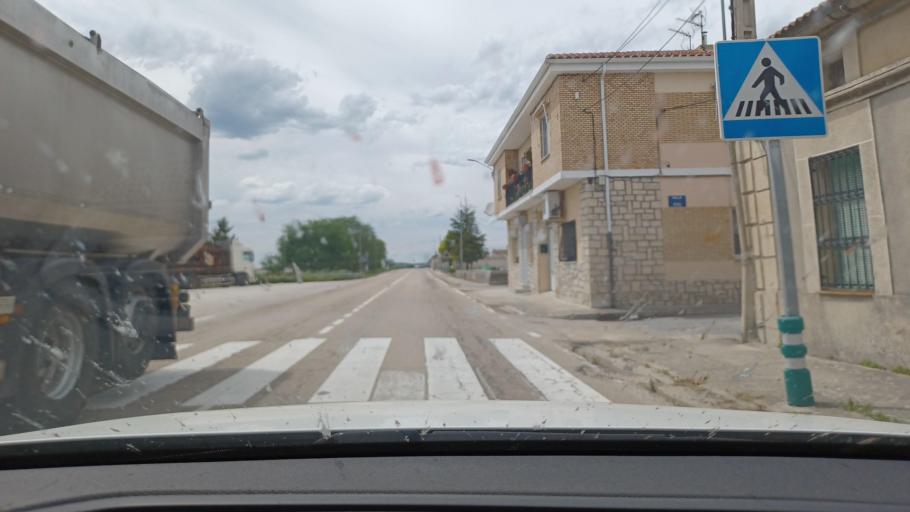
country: ES
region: Castille and Leon
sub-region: Provincia de Segovia
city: Frumales
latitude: 41.3836
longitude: -4.2389
